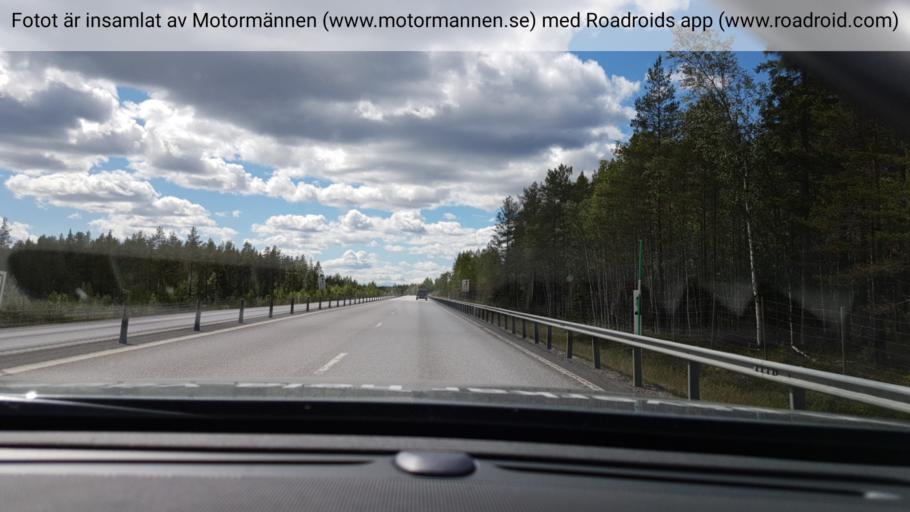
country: SE
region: Vaesterbotten
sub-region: Robertsfors Kommun
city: Robertsfors
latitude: 63.9916
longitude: 20.7572
